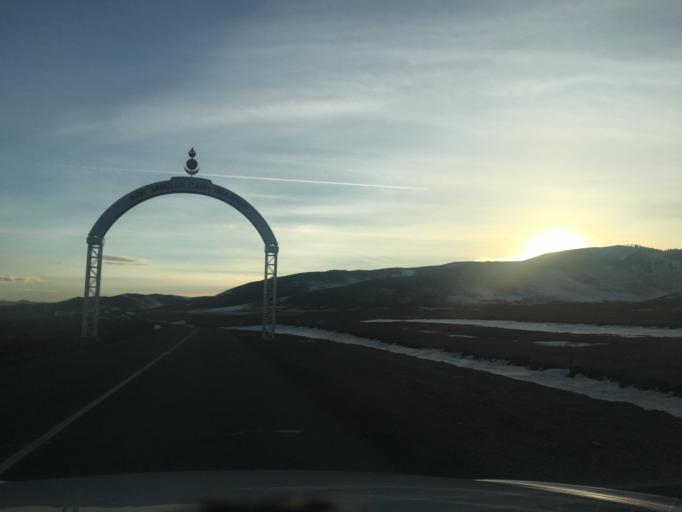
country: MN
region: Central Aimak
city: Mandal
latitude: 48.2324
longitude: 106.7206
